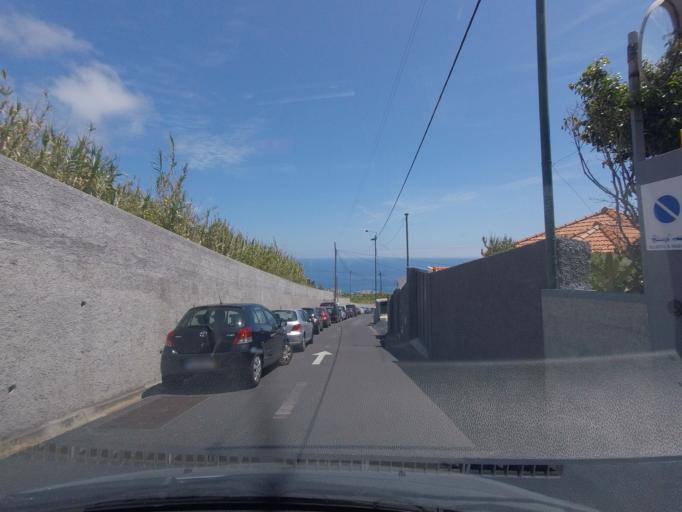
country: PT
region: Madeira
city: Camara de Lobos
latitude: 32.6515
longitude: -16.9501
